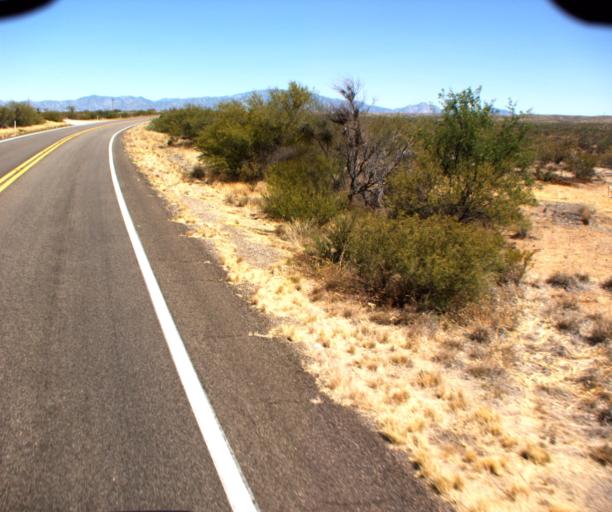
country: US
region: Arizona
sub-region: Pima County
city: Catalina
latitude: 32.6463
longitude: -111.0215
